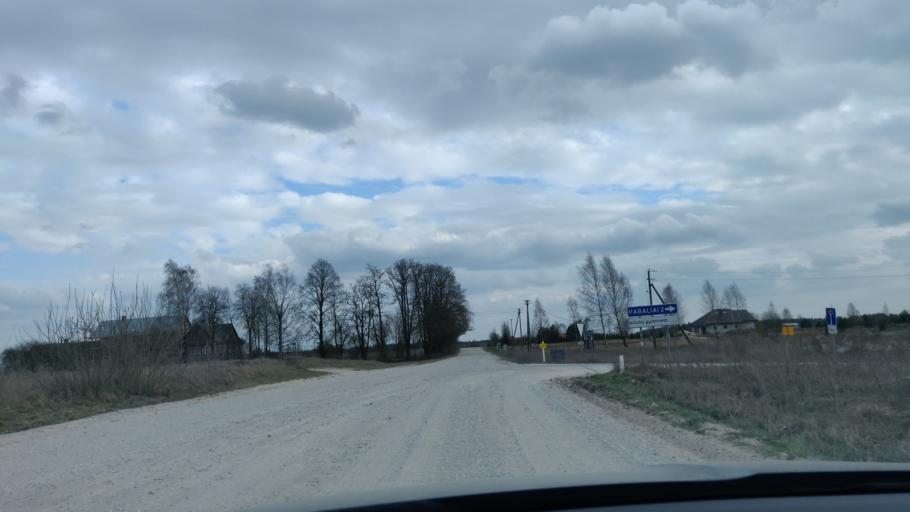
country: LT
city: Lentvaris
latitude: 54.6168
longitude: 25.0676
